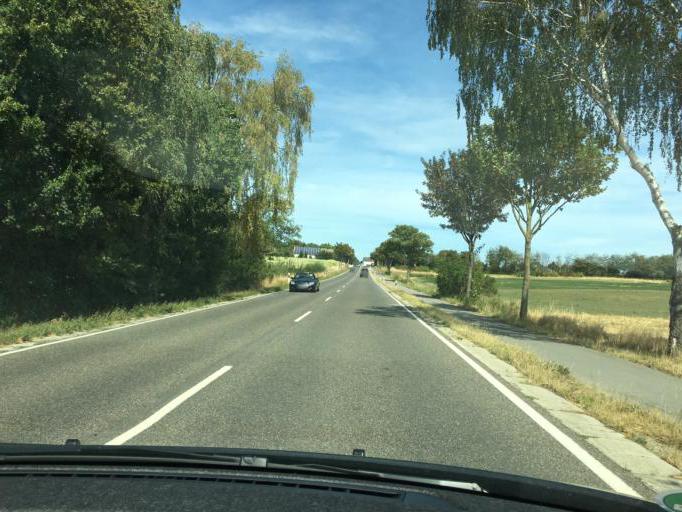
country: DE
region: North Rhine-Westphalia
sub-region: Regierungsbezirk Koln
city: Hurtgenwald
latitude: 50.7175
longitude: 6.3883
